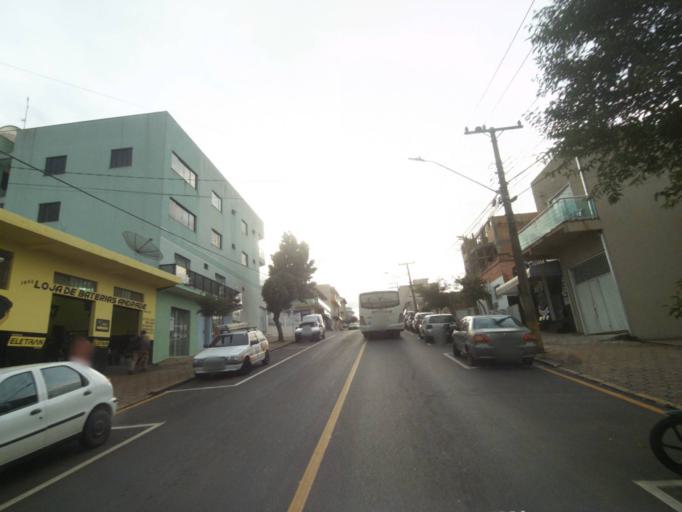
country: BR
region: Parana
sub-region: Telemaco Borba
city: Telemaco Borba
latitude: -24.3290
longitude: -50.6284
